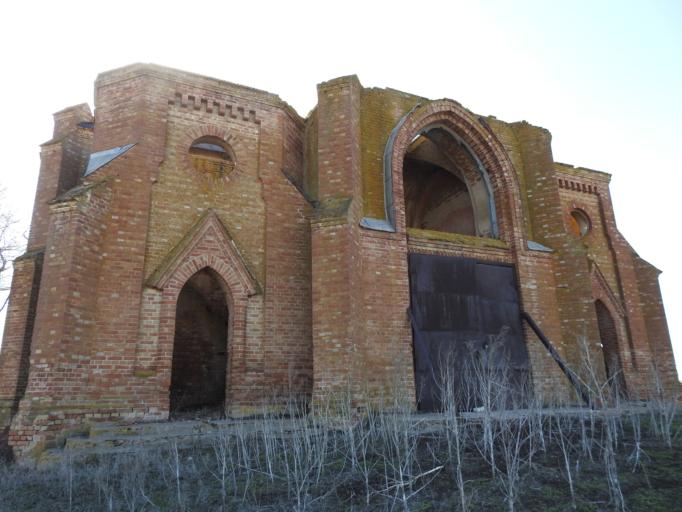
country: RU
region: Volgograd
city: Staraya Poltavka
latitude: 50.7807
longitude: 46.4148
